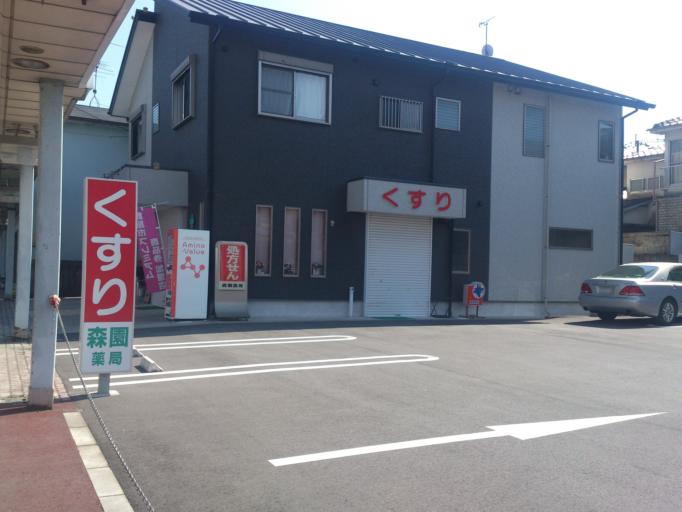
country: JP
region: Kagoshima
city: Kanoya
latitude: 31.3831
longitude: 130.8521
